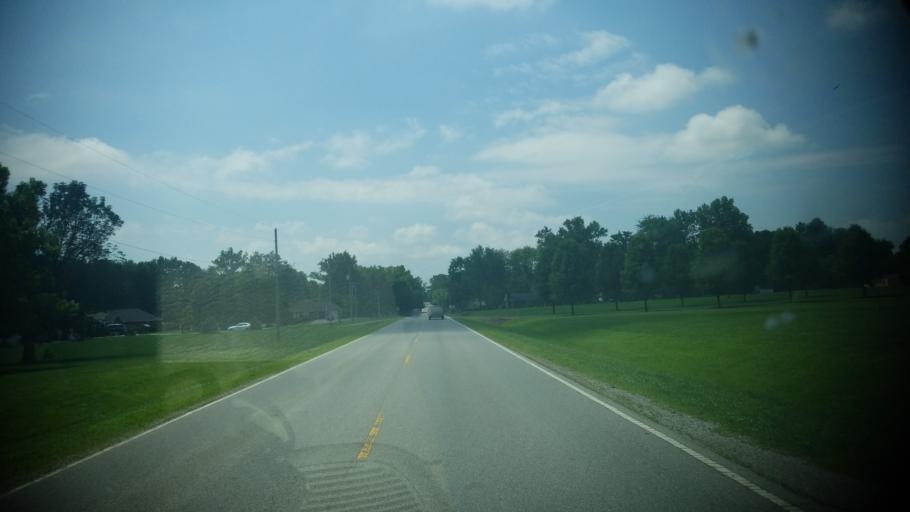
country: US
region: Illinois
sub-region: Wayne County
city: Fairfield
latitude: 38.3902
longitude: -88.3508
